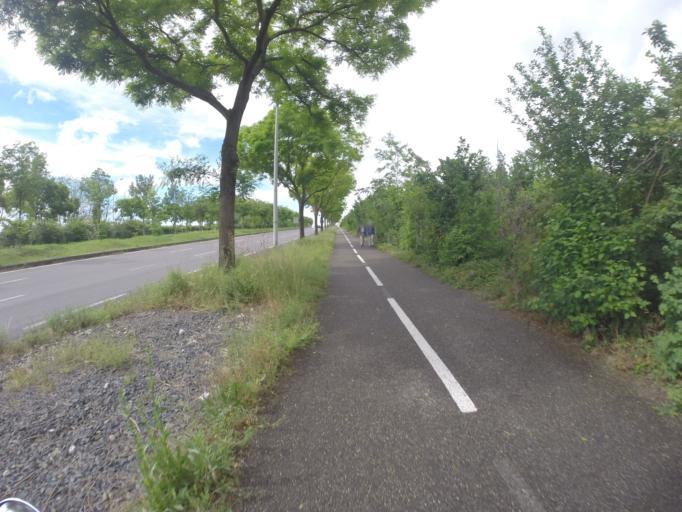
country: FR
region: Rhone-Alpes
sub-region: Departement du Rhone
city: Bron
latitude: 45.7296
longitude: 4.9290
